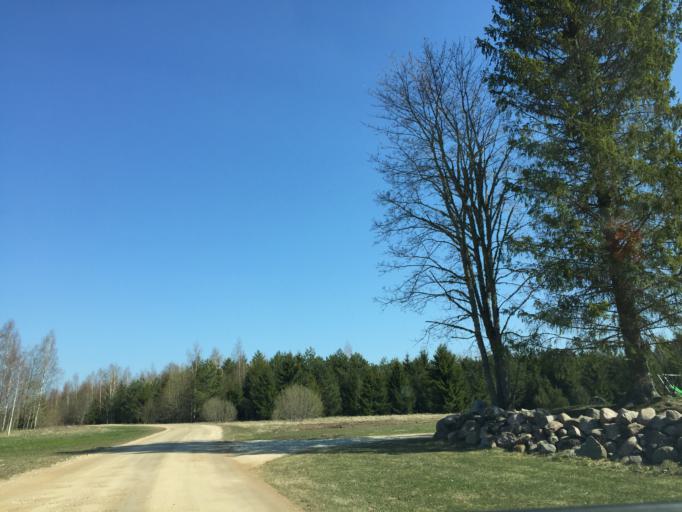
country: EE
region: Tartu
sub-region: Alatskivi vald
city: Kallaste
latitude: 58.5307
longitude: 26.9434
